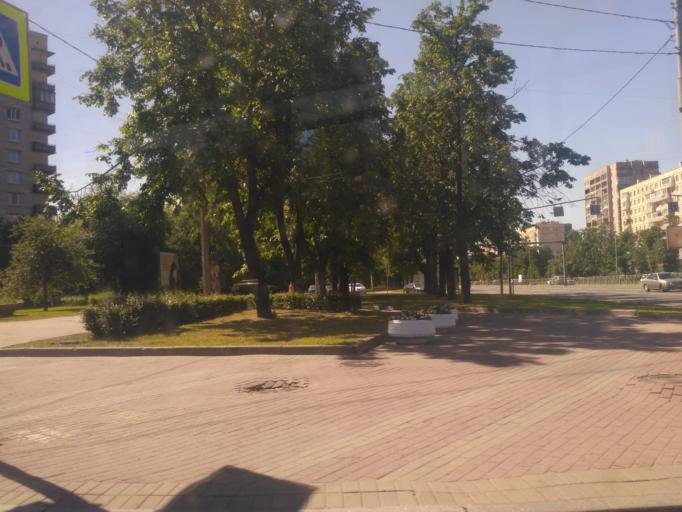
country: RU
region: Leningrad
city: Kalininskiy
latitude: 59.9683
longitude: 30.4111
